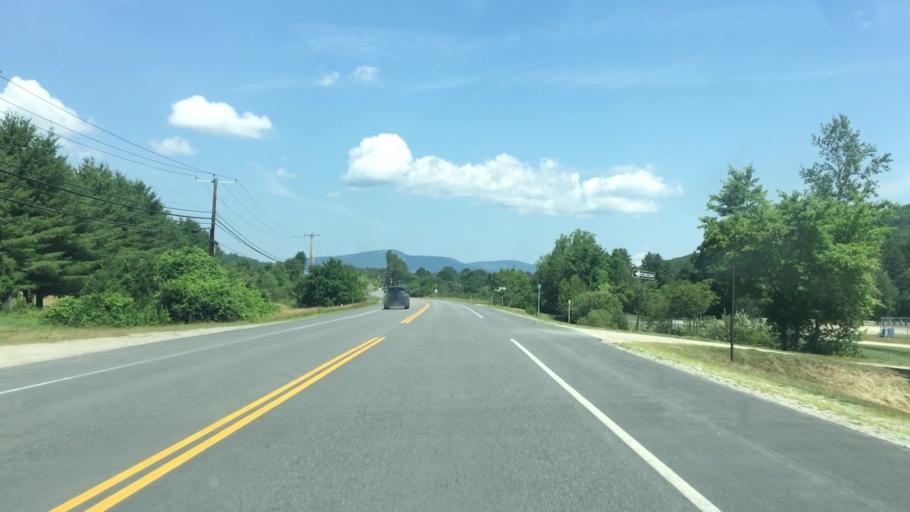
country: US
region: New Hampshire
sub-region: Sullivan County
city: Newport
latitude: 43.3792
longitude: -72.1800
